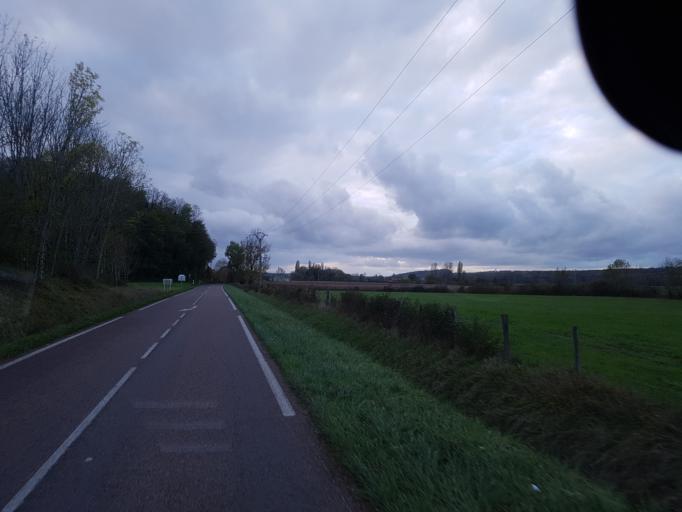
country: FR
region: Franche-Comte
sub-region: Departement du Jura
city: Arbois
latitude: 46.9158
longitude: 5.7531
